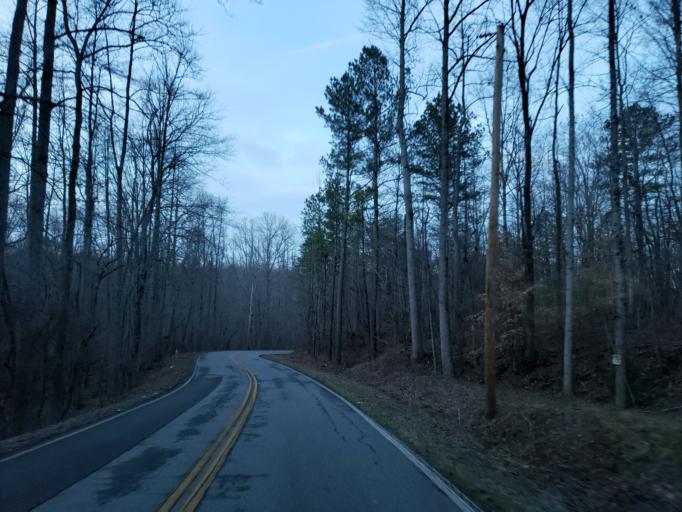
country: US
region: Georgia
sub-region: Cherokee County
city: Ball Ground
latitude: 34.2452
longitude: -84.3355
